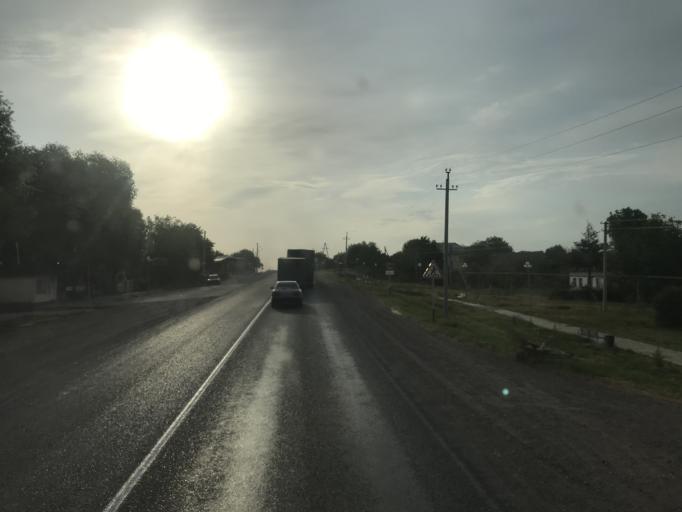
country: UZ
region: Toshkent
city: Salor
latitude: 41.4938
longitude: 69.3196
